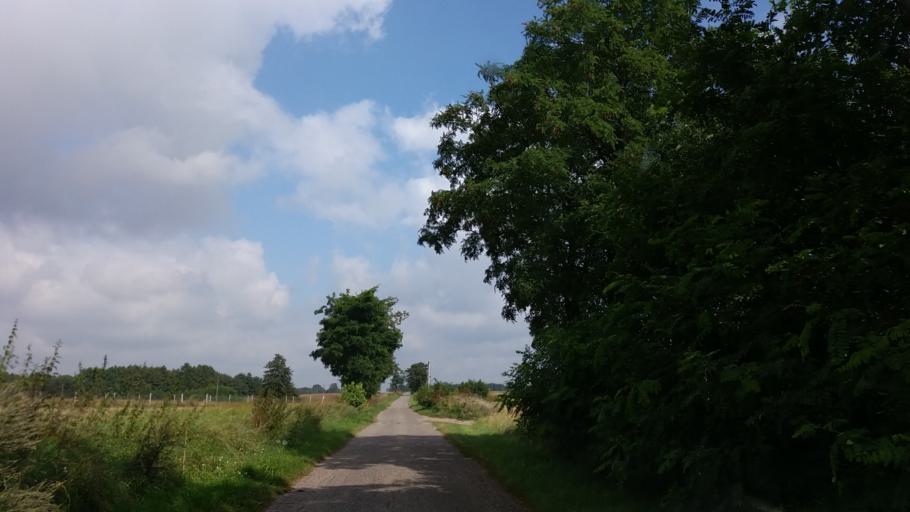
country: PL
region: West Pomeranian Voivodeship
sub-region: Powiat choszczenski
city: Krzecin
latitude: 53.0924
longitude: 15.4870
